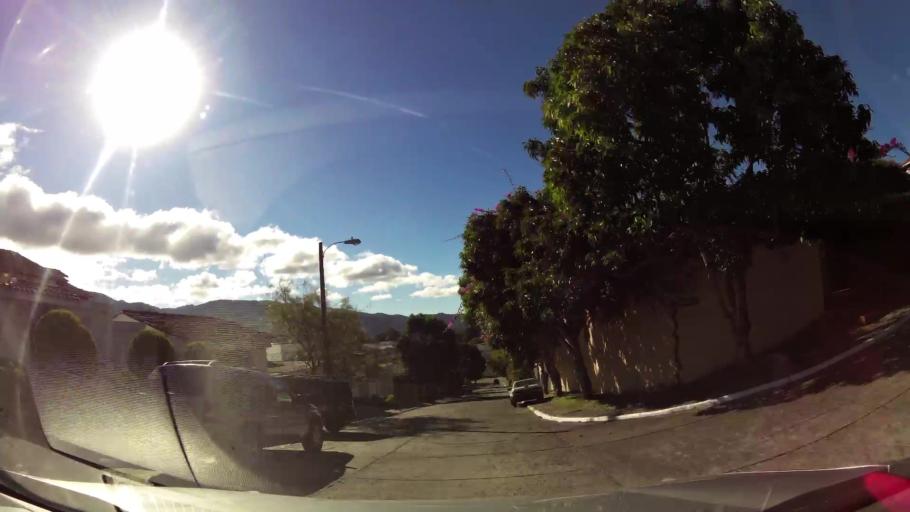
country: GT
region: Guatemala
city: Santa Catarina Pinula
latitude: 14.5671
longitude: -90.5257
